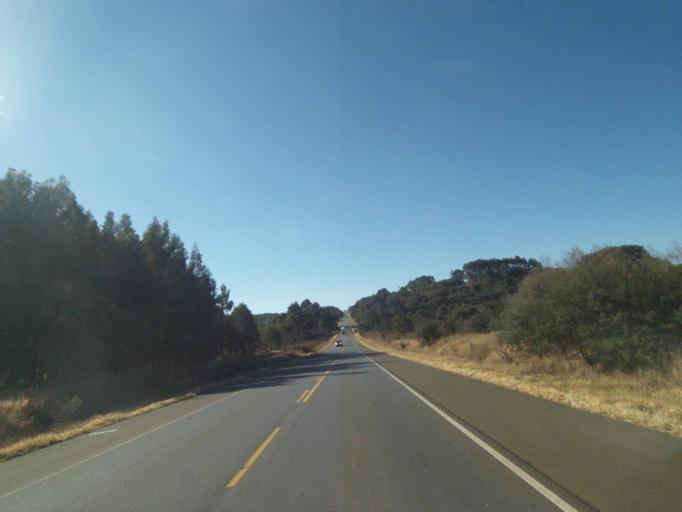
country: BR
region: Parana
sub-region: Tibagi
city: Tibagi
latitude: -24.6133
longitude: -50.4455
